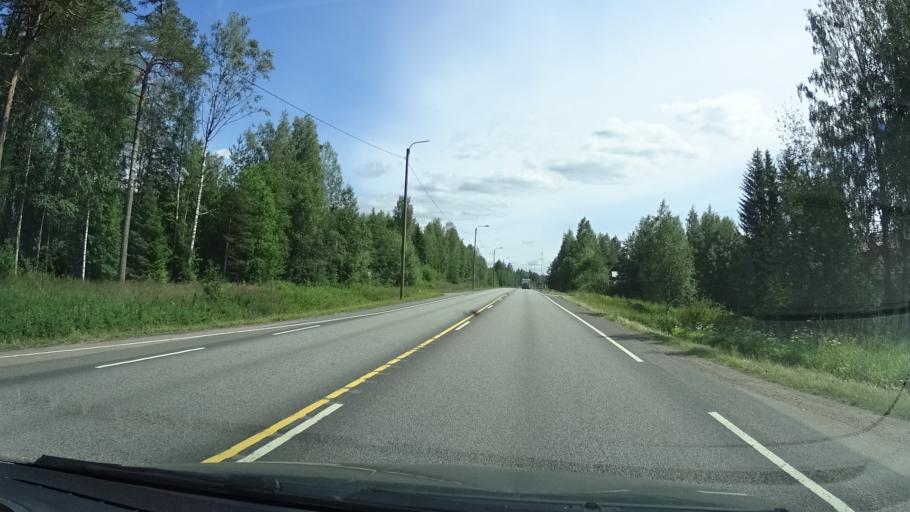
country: FI
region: Central Finland
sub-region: Jyvaeskylae
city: Uurainen
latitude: 62.2658
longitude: 25.4502
